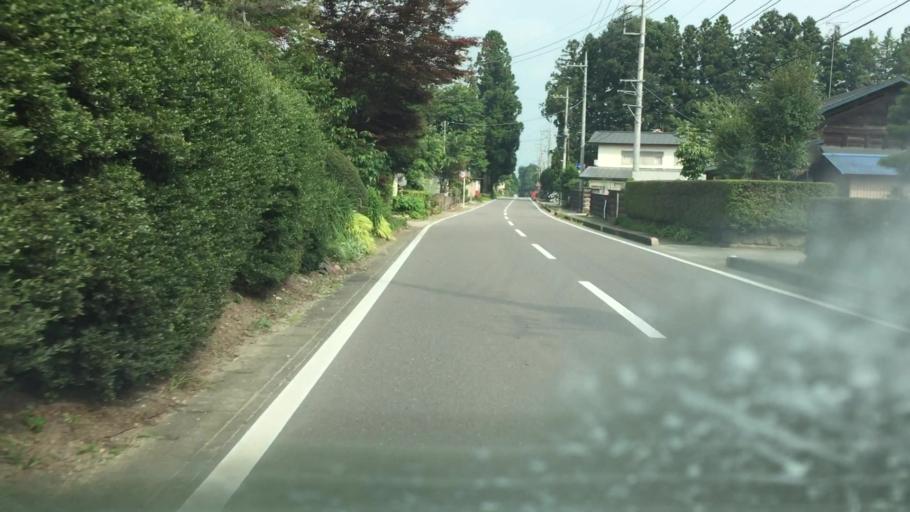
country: JP
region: Tochigi
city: Kuroiso
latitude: 36.9758
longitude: 139.9596
